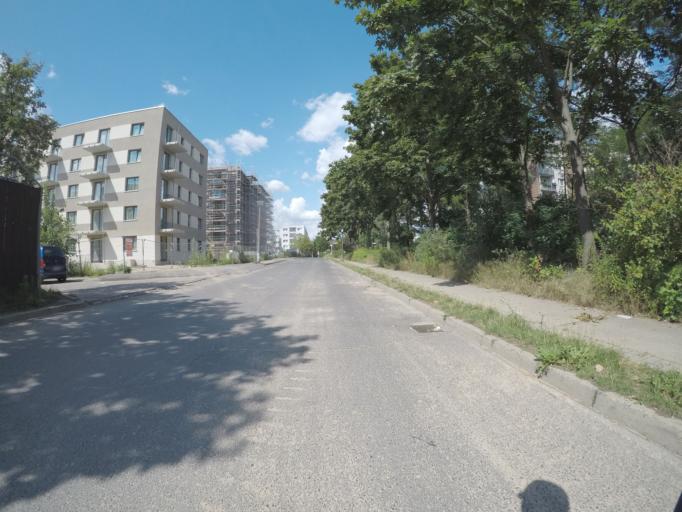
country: DE
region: Berlin
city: Kaulsdorf
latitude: 52.5167
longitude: 13.5826
